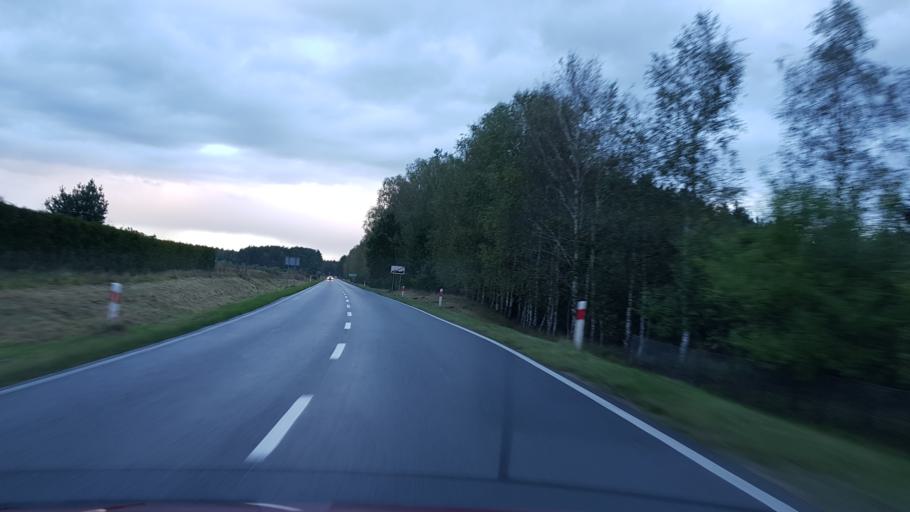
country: PL
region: Greater Poland Voivodeship
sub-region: Powiat pilski
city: Smilowo
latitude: 53.2279
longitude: 16.8769
